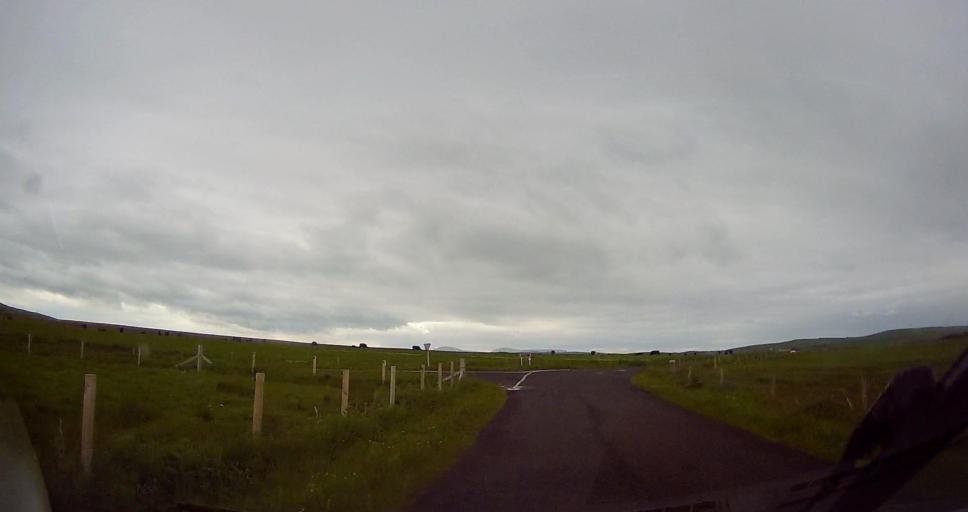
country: GB
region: Scotland
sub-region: Orkney Islands
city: Stromness
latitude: 59.1039
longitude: -3.2573
